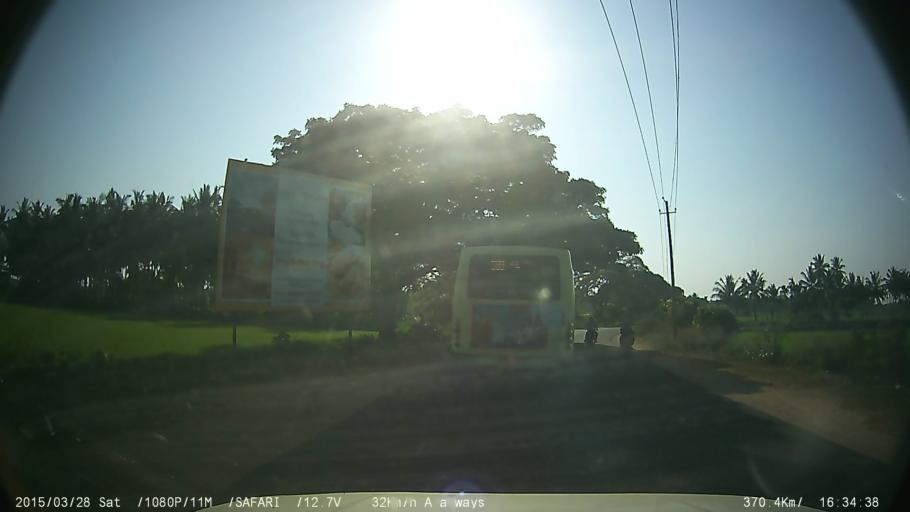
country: IN
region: Karnataka
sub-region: Mandya
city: Shrirangapattana
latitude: 12.3916
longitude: 76.6171
